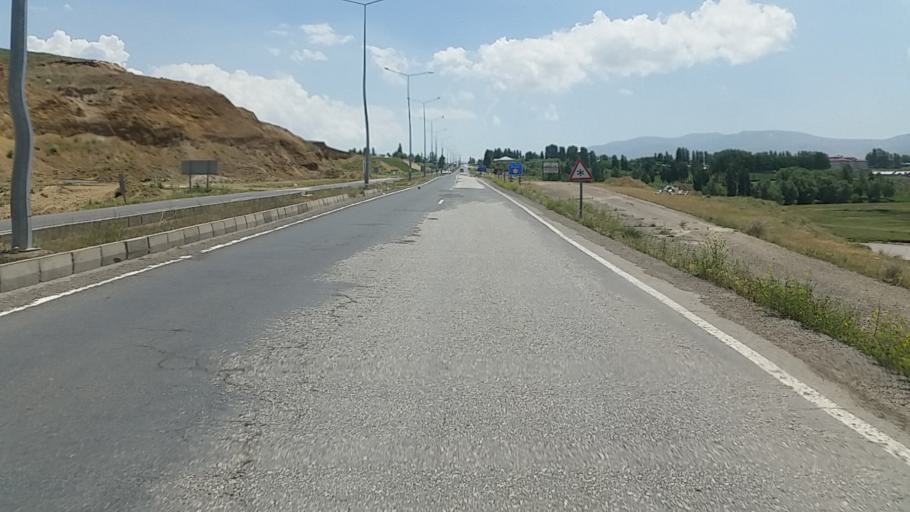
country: TR
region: Agri
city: Taslicay
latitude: 39.6480
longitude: 43.3650
